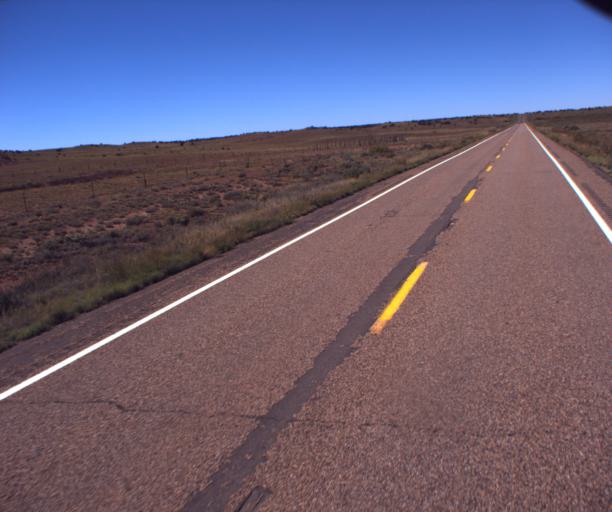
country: US
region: Arizona
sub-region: Apache County
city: Saint Johns
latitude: 34.5902
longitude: -109.5997
